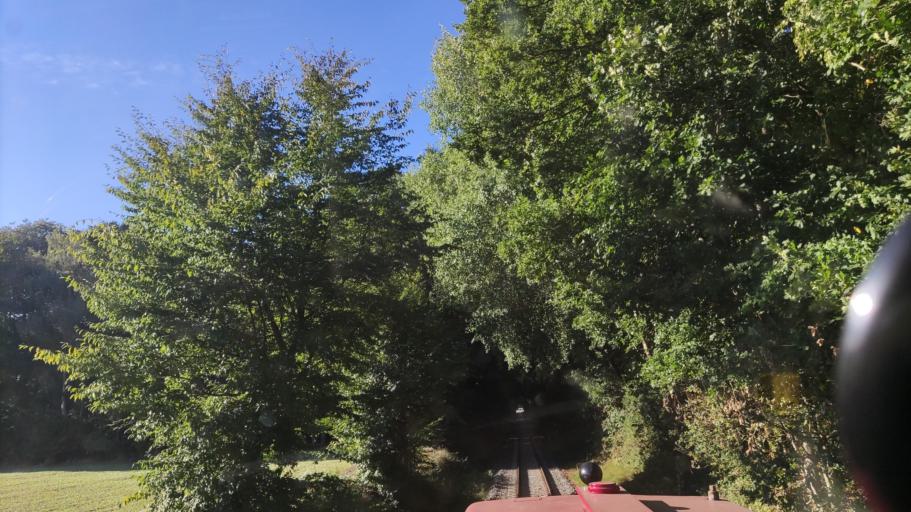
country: DE
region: Lower Saxony
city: Melbeck
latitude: 53.2082
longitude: 10.3802
